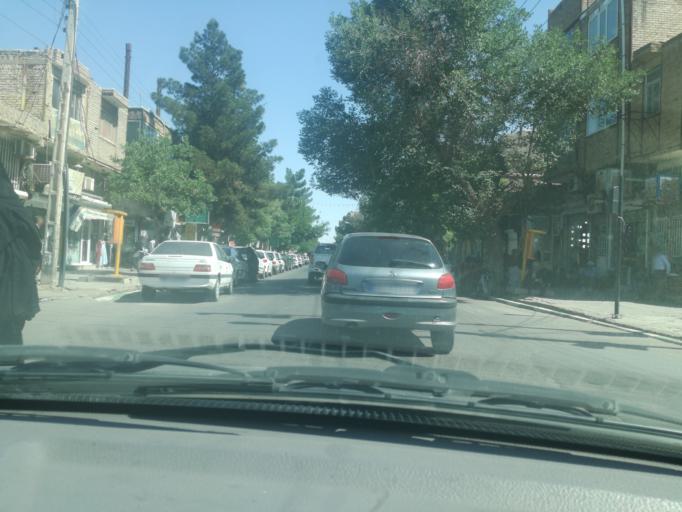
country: IR
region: Razavi Khorasan
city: Sarakhs
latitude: 36.5368
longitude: 61.1632
